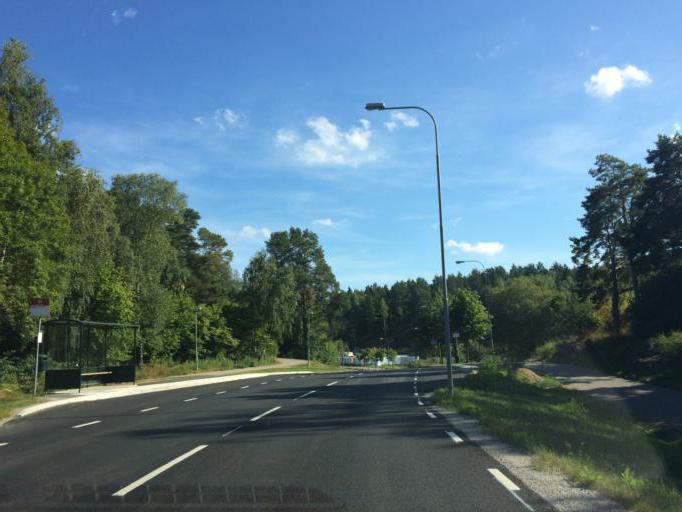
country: SE
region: Stockholm
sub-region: Upplands Vasby Kommun
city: Upplands Vaesby
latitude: 59.4979
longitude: 17.9329
